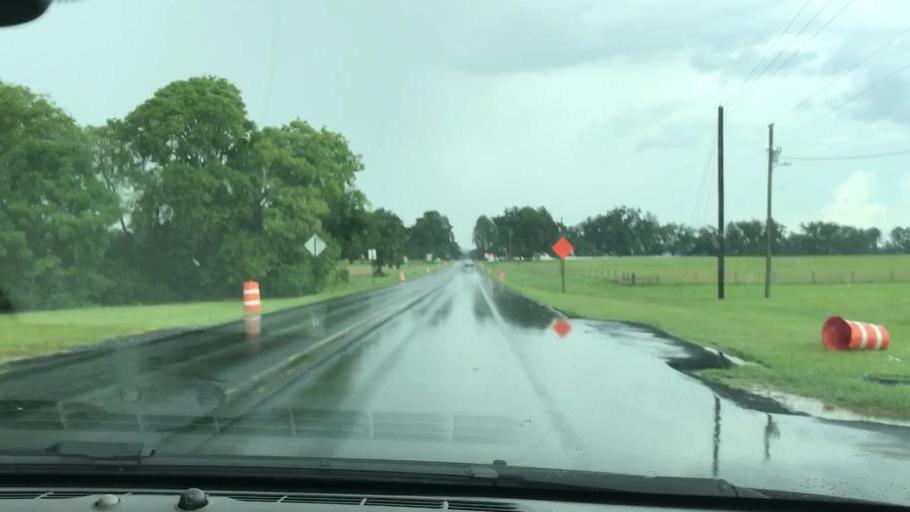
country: US
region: Georgia
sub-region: Clay County
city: Fort Gaines
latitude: 31.5395
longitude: -85.0208
